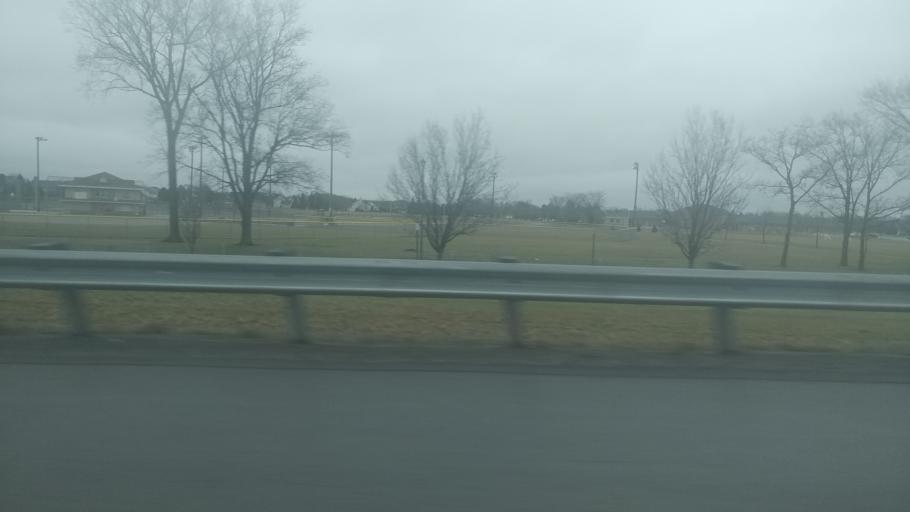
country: US
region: Ohio
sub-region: Lucas County
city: Maumee
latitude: 41.5328
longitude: -83.6590
